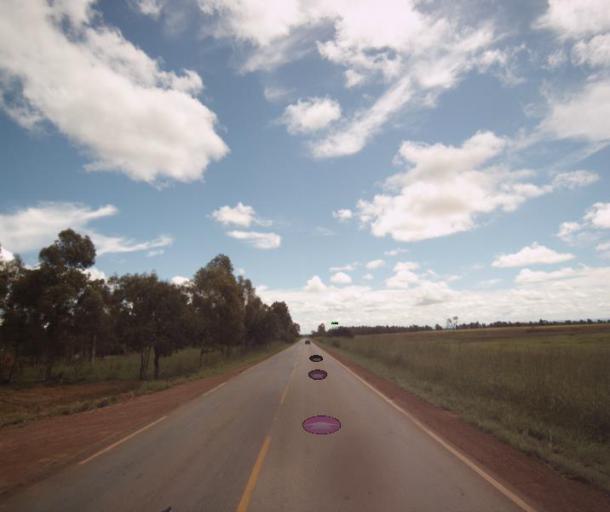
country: BR
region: Goias
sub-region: Padre Bernardo
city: Padre Bernardo
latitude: -15.3877
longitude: -48.2063
